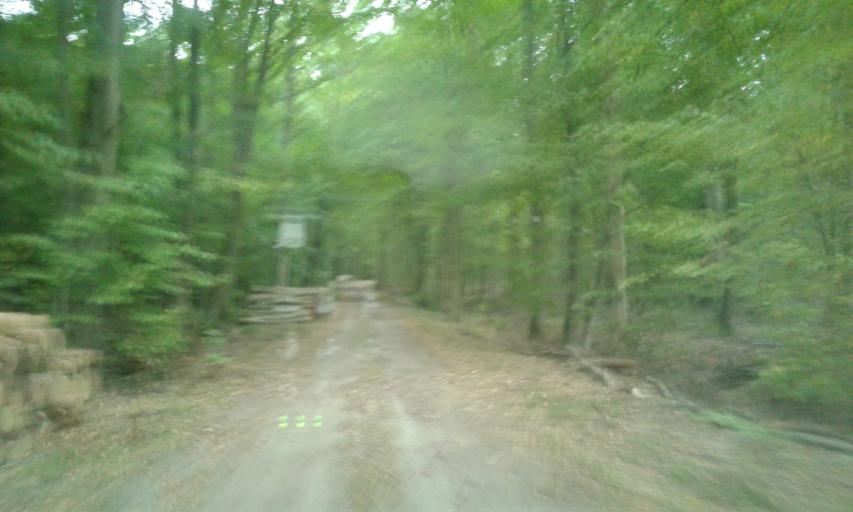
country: PL
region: West Pomeranian Voivodeship
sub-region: Powiat stargardzki
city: Dolice
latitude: 53.1843
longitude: 15.2446
